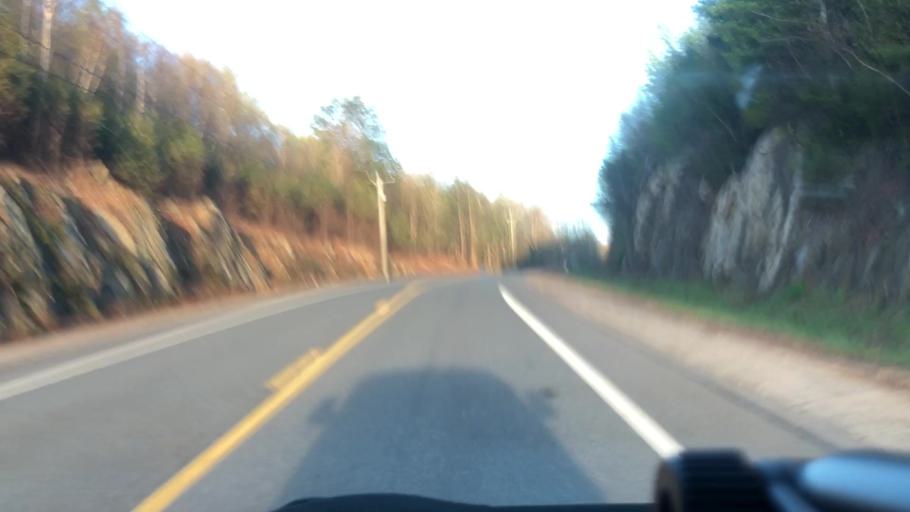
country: US
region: Massachusetts
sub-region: Hampshire County
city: Westhampton
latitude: 42.2830
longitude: -72.8146
